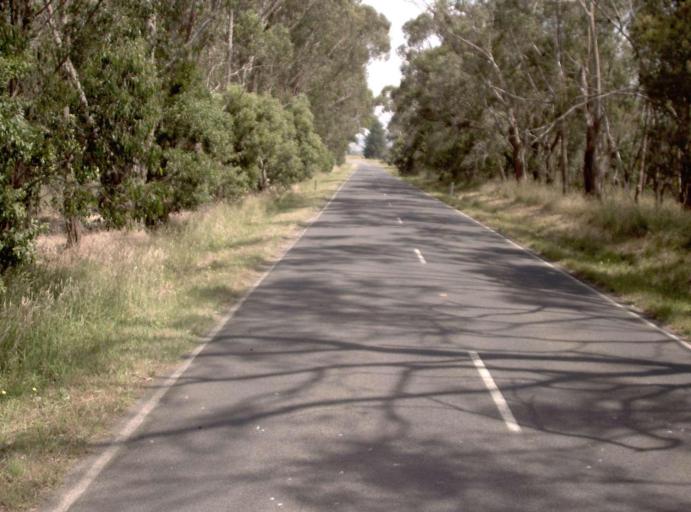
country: AU
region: Victoria
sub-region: Latrobe
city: Traralgon
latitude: -38.2621
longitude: 146.5465
